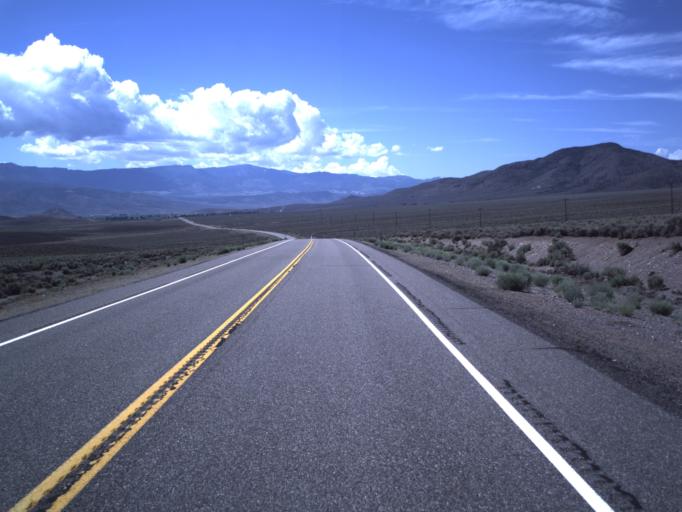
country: US
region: Utah
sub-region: Piute County
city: Junction
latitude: 38.2953
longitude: -112.2252
